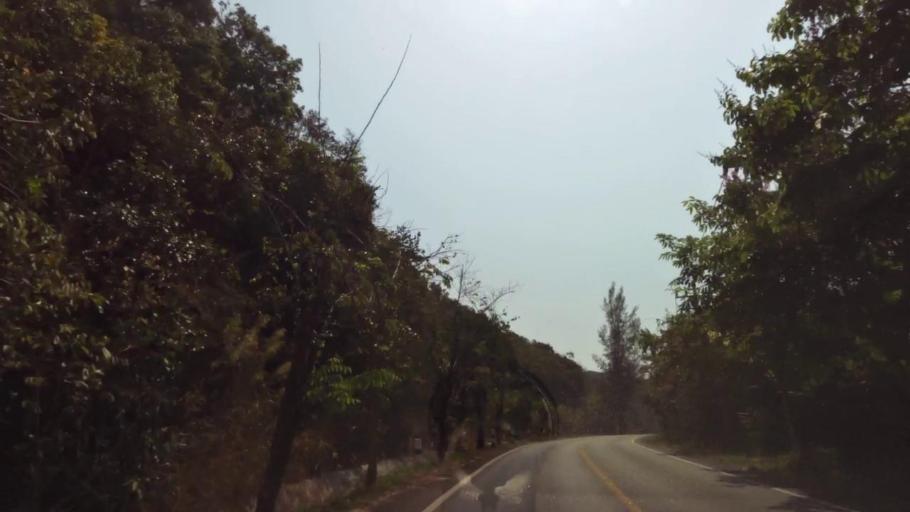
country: TH
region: Chanthaburi
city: Tha Mai
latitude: 12.5264
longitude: 101.9473
